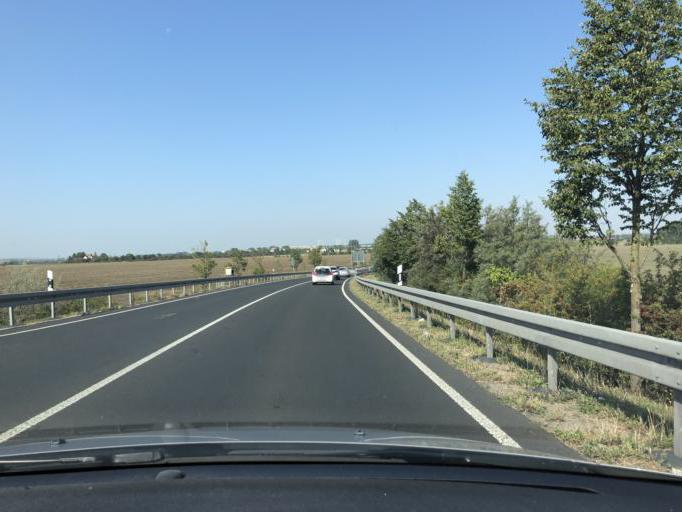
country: DE
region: Thuringia
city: Sprotau
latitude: 51.1558
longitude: 11.1678
